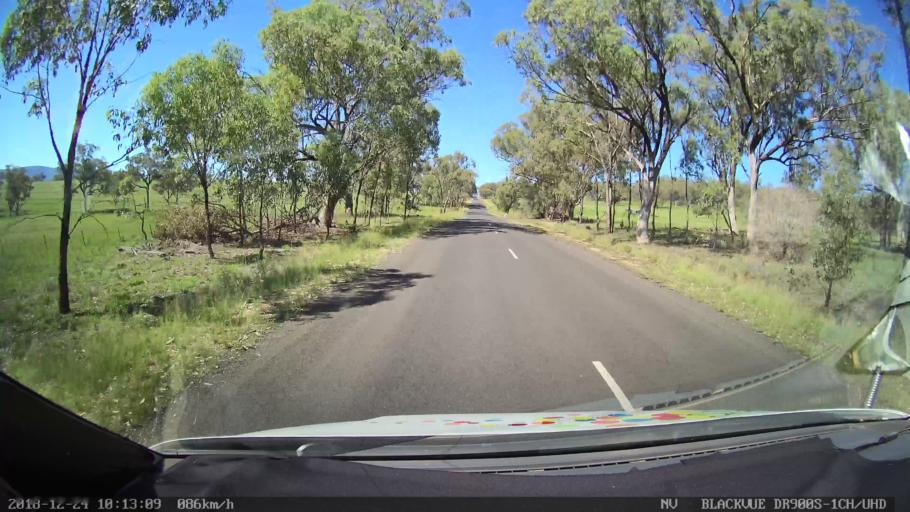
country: AU
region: New South Wales
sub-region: Liverpool Plains
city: Quirindi
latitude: -31.6866
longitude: 150.6419
